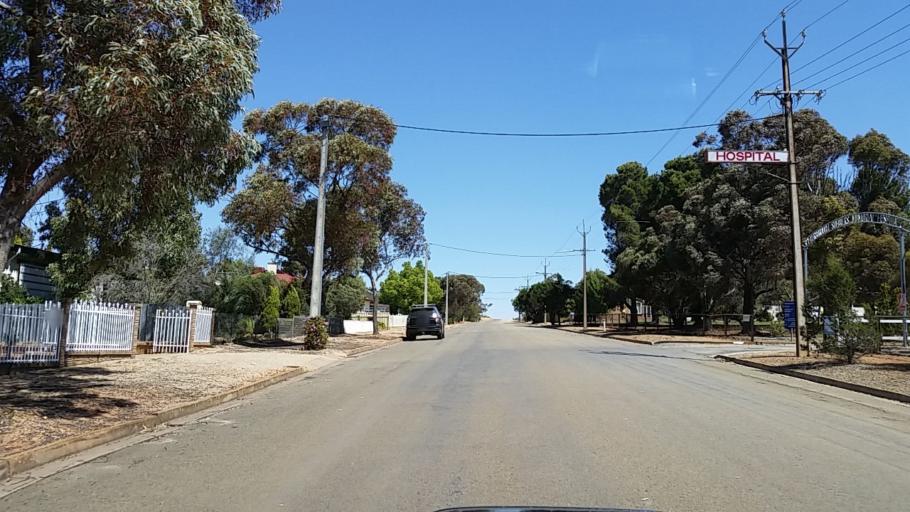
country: AU
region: South Australia
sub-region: Peterborough
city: Peterborough
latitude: -32.9796
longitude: 138.8318
